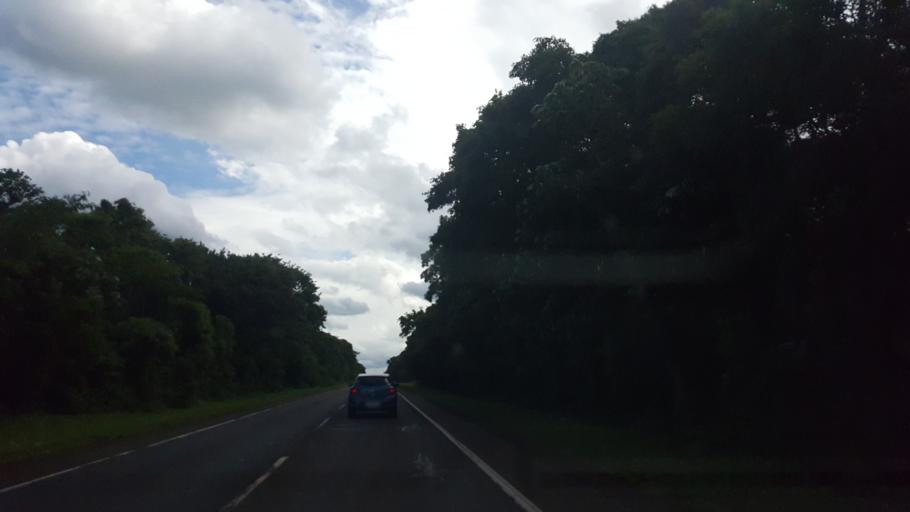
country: AR
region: Misiones
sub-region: Departamento de Iguazu
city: Puerto Iguazu
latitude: -25.7083
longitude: -54.5167
